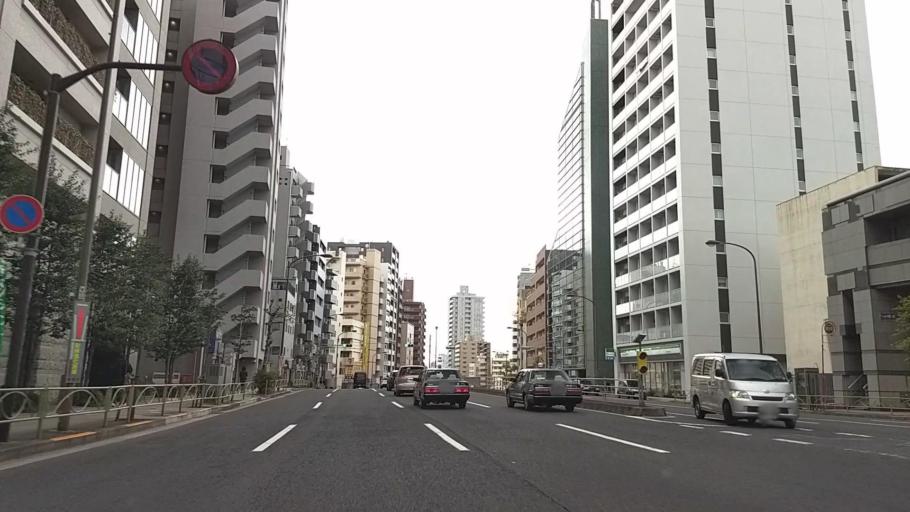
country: JP
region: Tokyo
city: Tokyo
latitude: 35.6310
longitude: 139.7296
